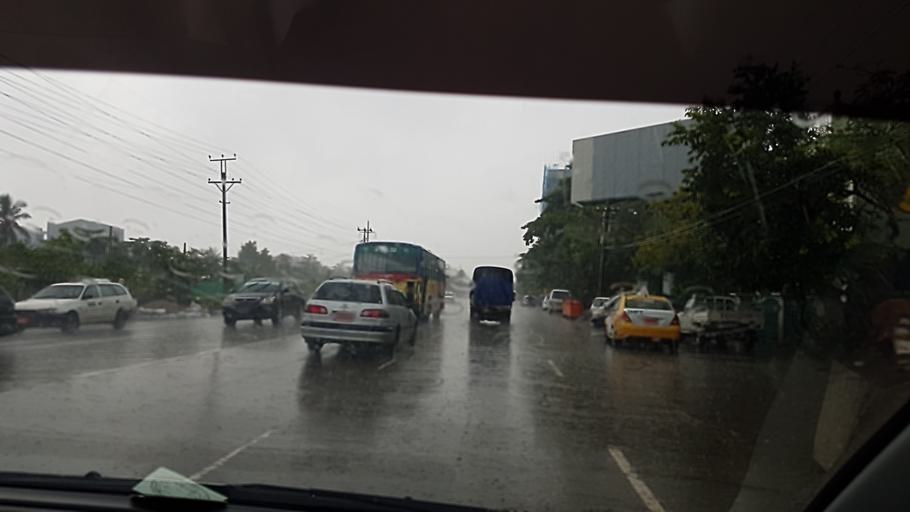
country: MM
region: Yangon
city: Yangon
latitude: 16.7797
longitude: 96.1915
